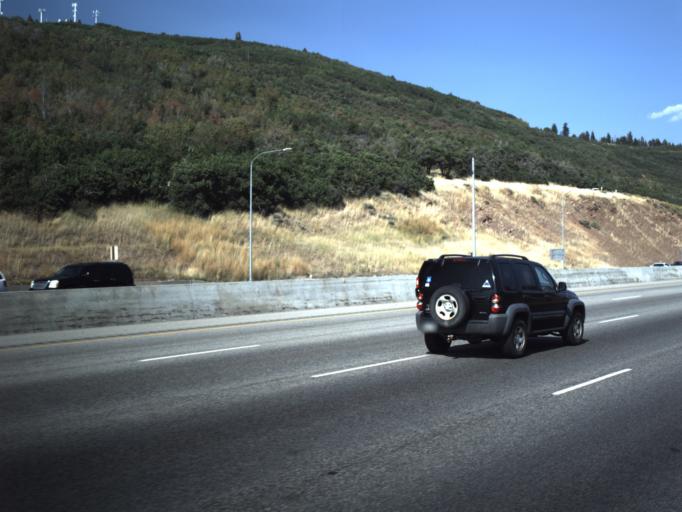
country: US
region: Utah
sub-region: Summit County
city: Summit Park
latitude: 40.7529
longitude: -111.6254
